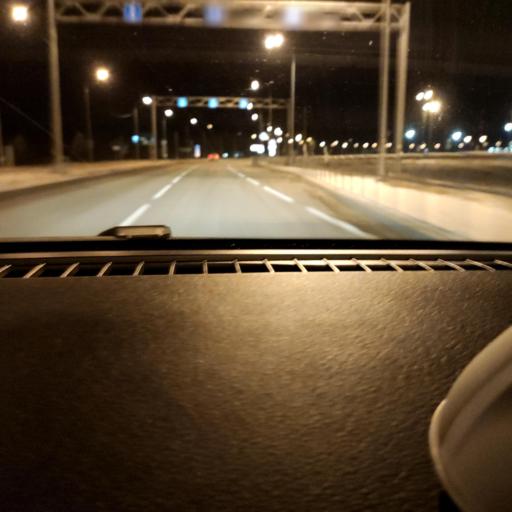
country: RU
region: Samara
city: Samara
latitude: 53.2703
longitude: 50.2352
